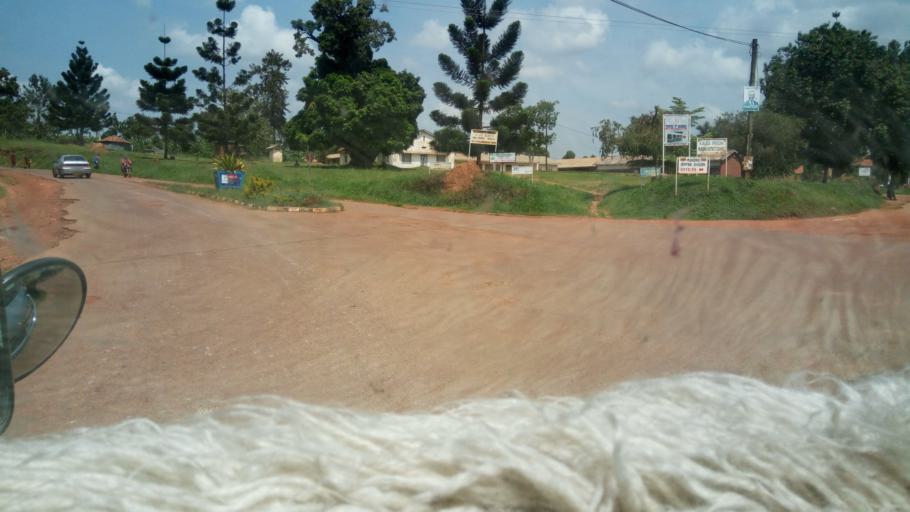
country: UG
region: Central Region
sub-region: Mukono District
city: Mukono
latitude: 0.3609
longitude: 32.7425
